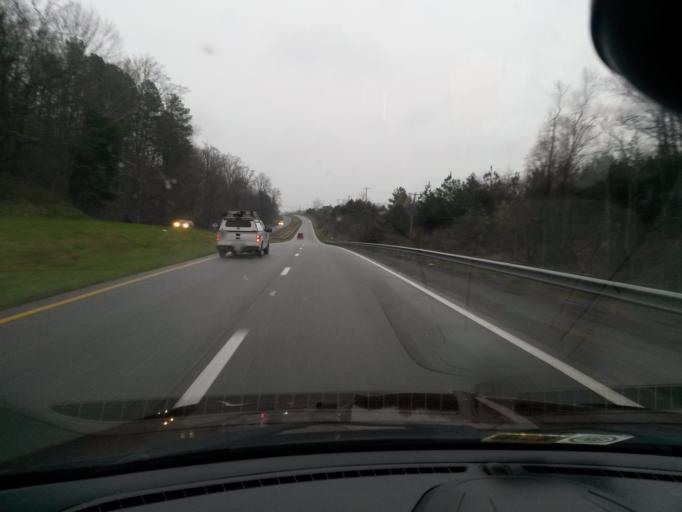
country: US
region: Virginia
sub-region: City of Bedford
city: Bedford
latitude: 37.3509
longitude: -79.6422
